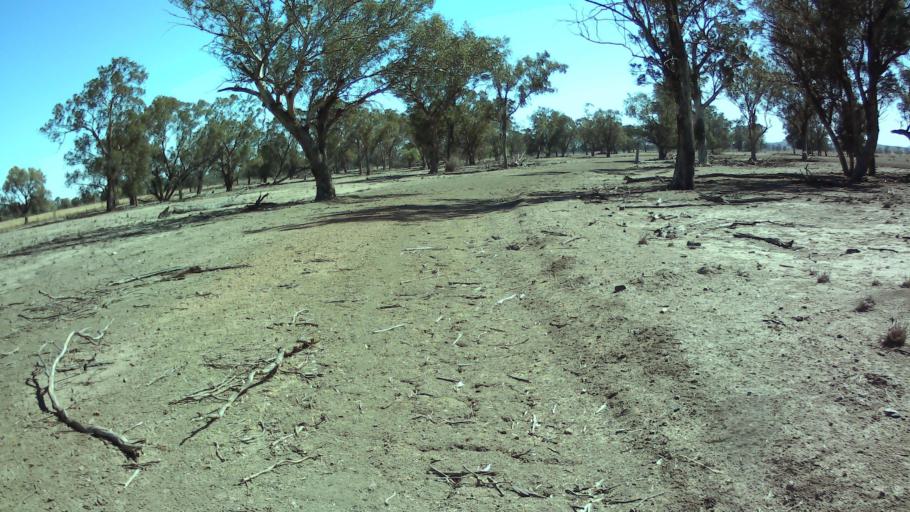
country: AU
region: New South Wales
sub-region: Bland
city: West Wyalong
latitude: -33.7659
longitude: 147.6575
